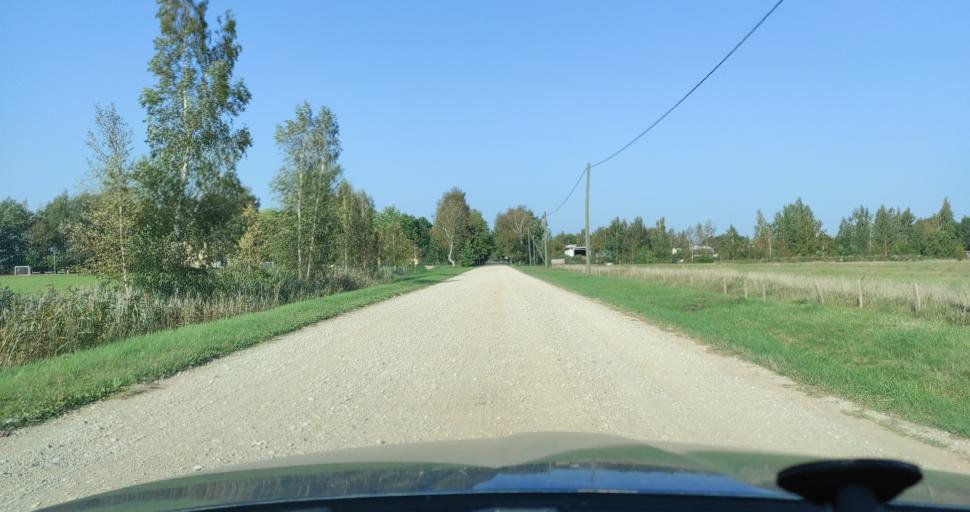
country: LV
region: Ventspils Rajons
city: Piltene
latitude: 57.2240
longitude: 21.6112
